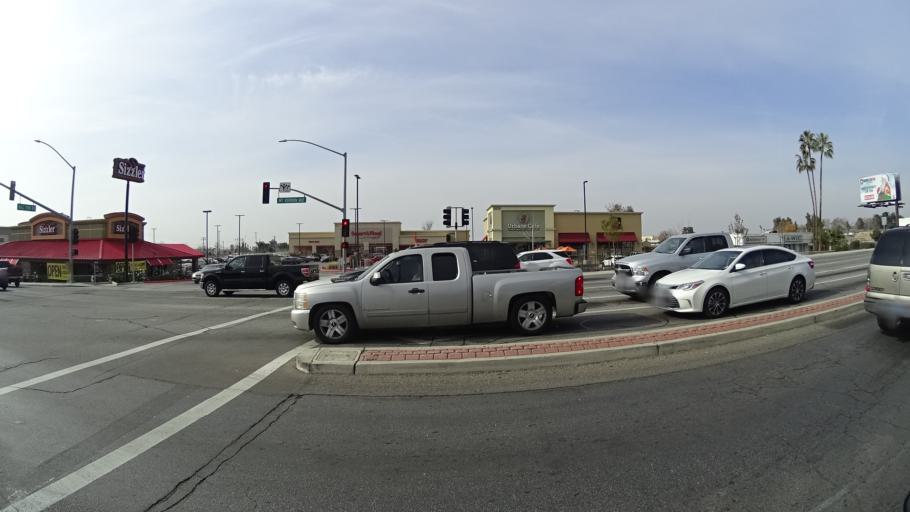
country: US
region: California
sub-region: Kern County
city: Bakersfield
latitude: 35.3929
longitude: -118.9673
